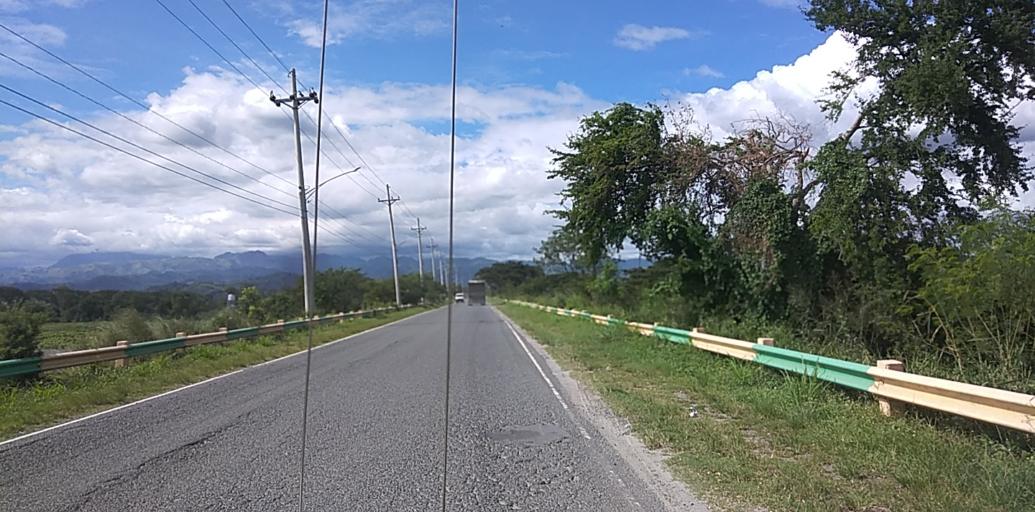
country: PH
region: Central Luzon
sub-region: Province of Pampanga
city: Porac
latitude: 15.0839
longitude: 120.5456
